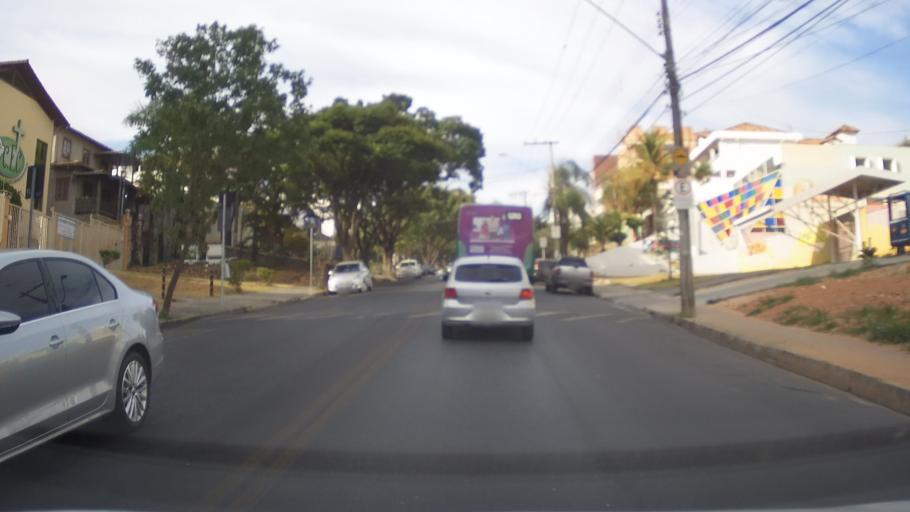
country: BR
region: Minas Gerais
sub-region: Belo Horizonte
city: Belo Horizonte
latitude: -19.8793
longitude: -43.9974
